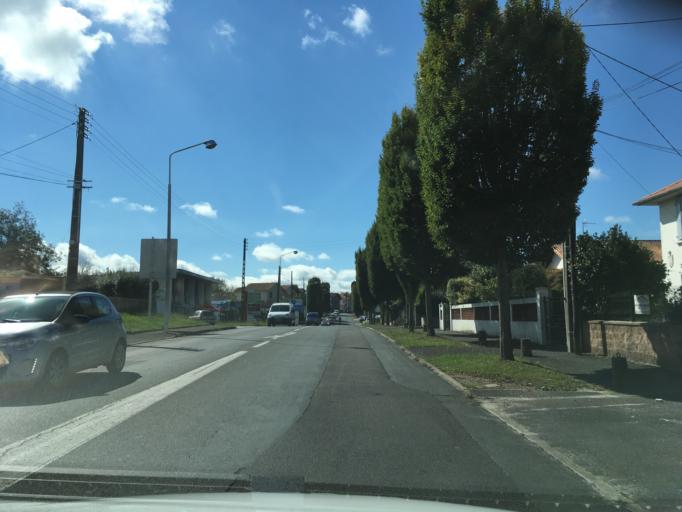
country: FR
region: Aquitaine
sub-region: Departement des Pyrenees-Atlantiques
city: Boucau
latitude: 43.5096
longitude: -1.4681
